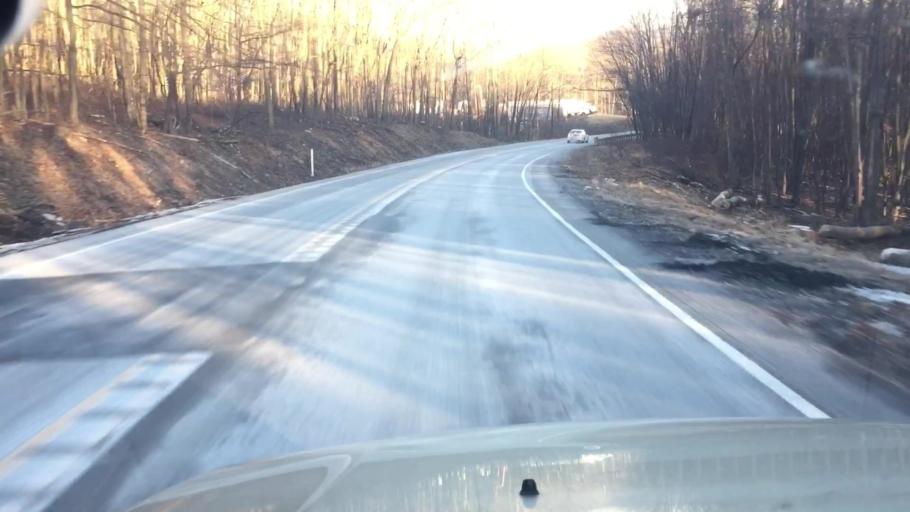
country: US
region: Pennsylvania
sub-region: Luzerne County
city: Conyngham
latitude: 41.0311
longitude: -76.0827
